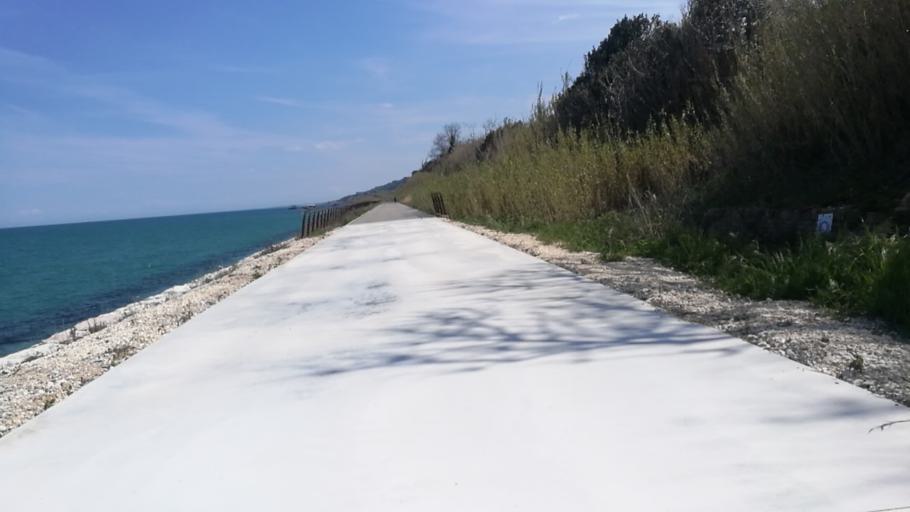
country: IT
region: Abruzzo
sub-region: Provincia di Chieti
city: Marina di San Vito
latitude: 42.3220
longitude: 14.4301
